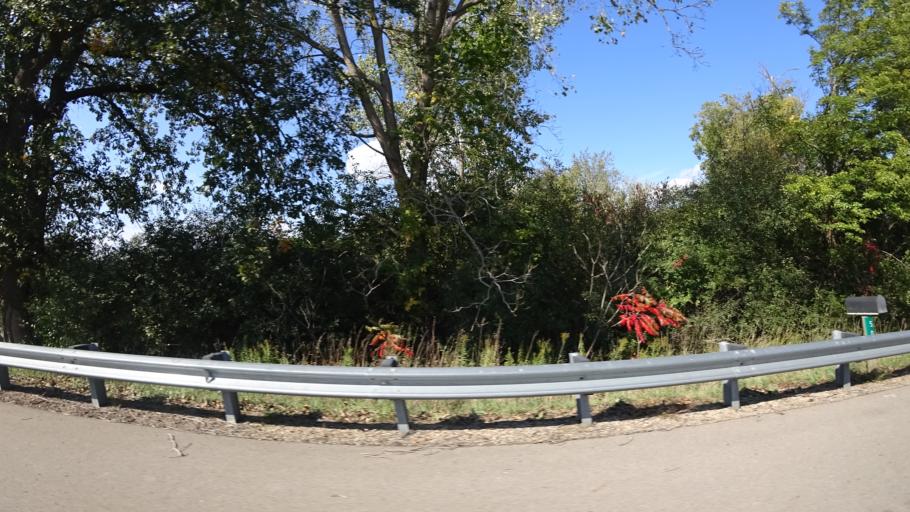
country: US
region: Michigan
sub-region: Jackson County
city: Concord
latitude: 42.1774
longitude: -84.6545
